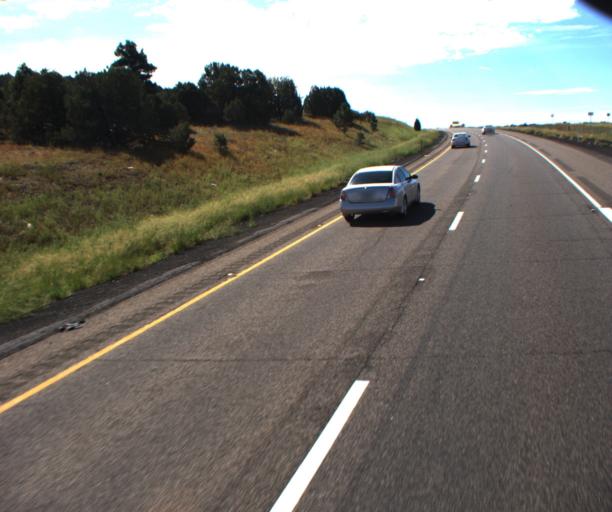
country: US
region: Arizona
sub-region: Yavapai County
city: Village of Oak Creek (Big Park)
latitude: 34.8147
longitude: -111.6123
